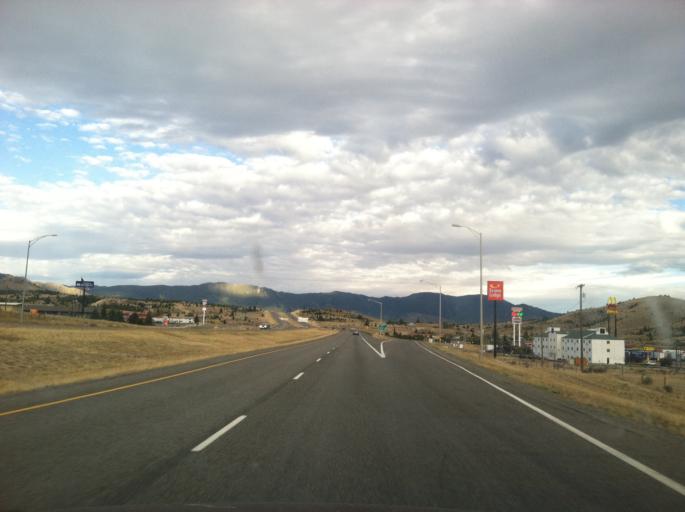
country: US
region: Montana
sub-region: Silver Bow County
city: Butte
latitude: 46.0075
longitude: -112.6184
